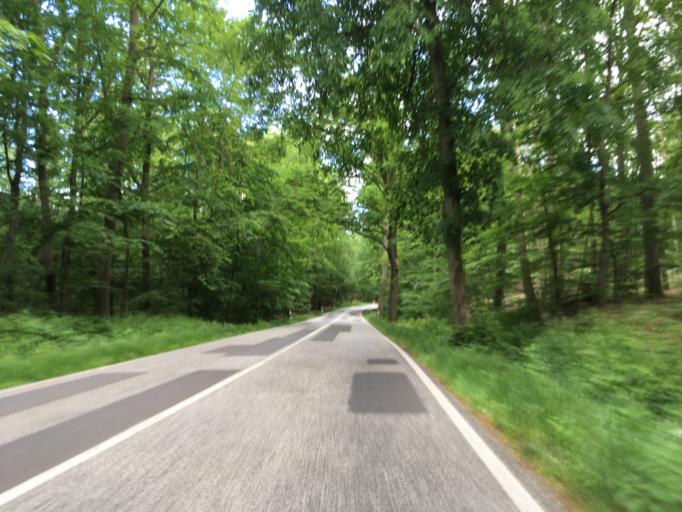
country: DE
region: Brandenburg
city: Bad Freienwalde
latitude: 52.7468
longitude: 13.9845
